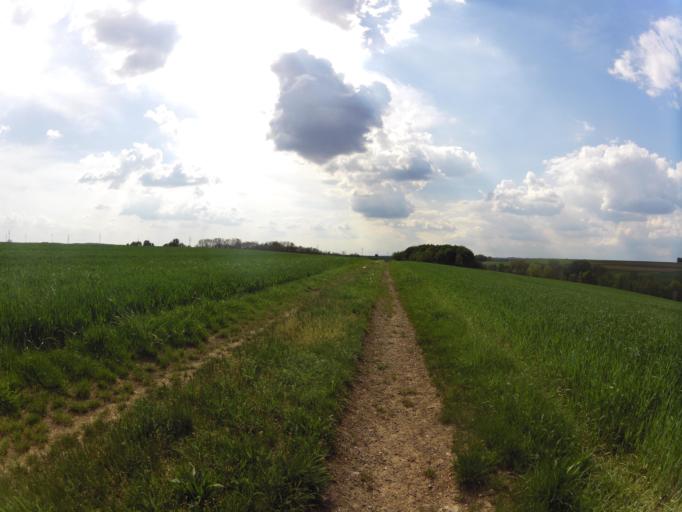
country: DE
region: Bavaria
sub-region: Regierungsbezirk Unterfranken
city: Giebelstadt
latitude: 49.6223
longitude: 9.9429
